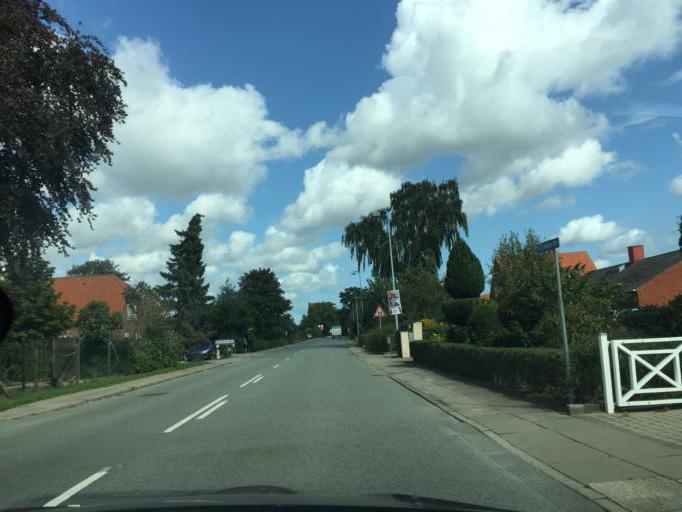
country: DK
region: South Denmark
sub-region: Odense Kommune
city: Stige
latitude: 55.4539
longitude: 10.3761
